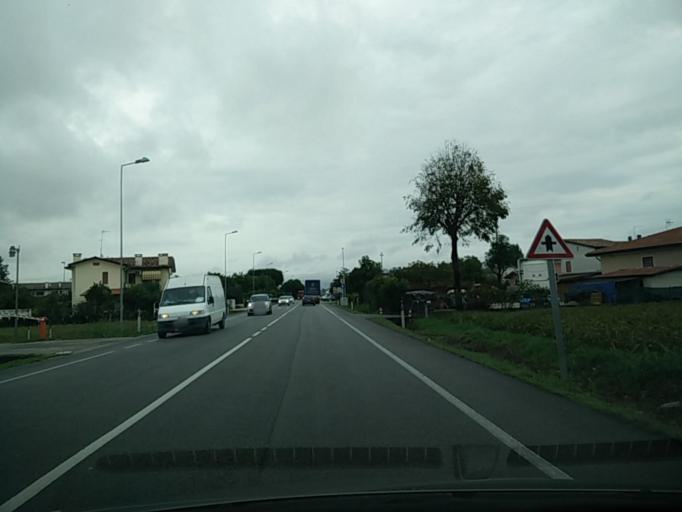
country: IT
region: Veneto
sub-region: Provincia di Padova
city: Galliera Veneta
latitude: 45.6671
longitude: 11.8433
